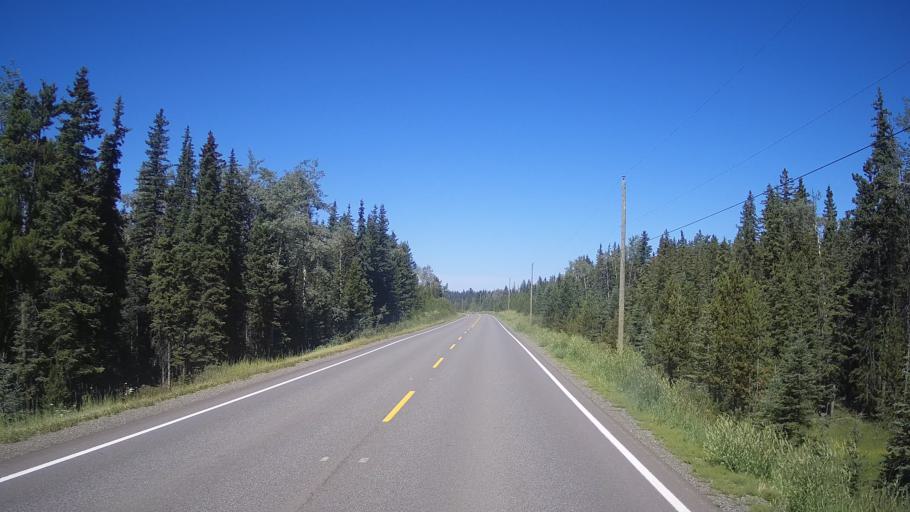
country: CA
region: British Columbia
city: Cache Creek
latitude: 51.5448
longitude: -121.0667
